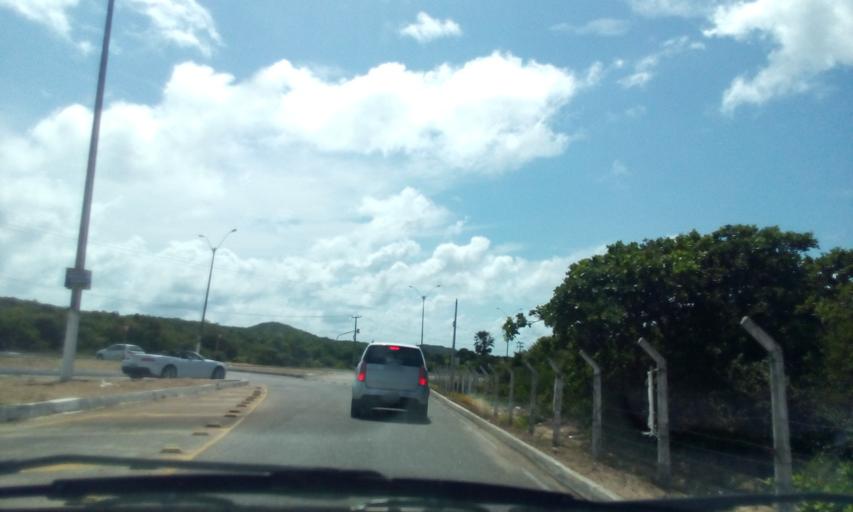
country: BR
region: Rio Grande do Norte
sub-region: Parnamirim
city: Parnamirim
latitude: -5.8945
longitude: -35.1789
